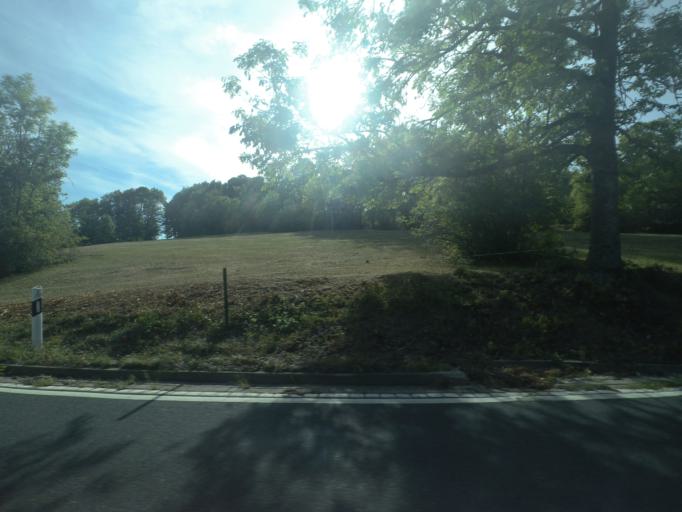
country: DE
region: Thuringia
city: Stepfershausen
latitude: 50.5827
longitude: 10.2829
